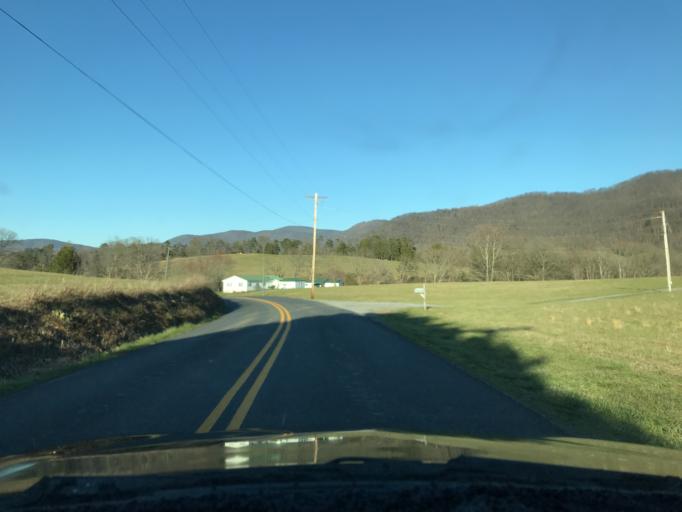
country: US
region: Virginia
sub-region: Botetourt County
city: Blue Ridge
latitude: 37.4096
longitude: -79.7048
